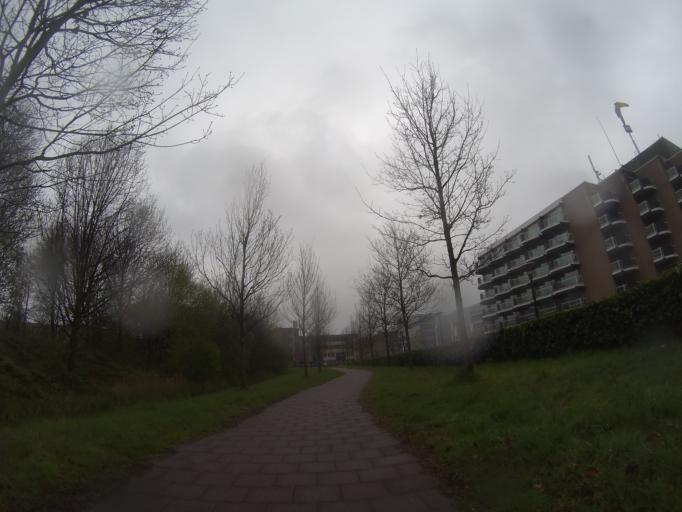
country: NL
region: Utrecht
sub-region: Gemeente Amersfoort
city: Randenbroek
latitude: 52.1444
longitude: 5.4172
